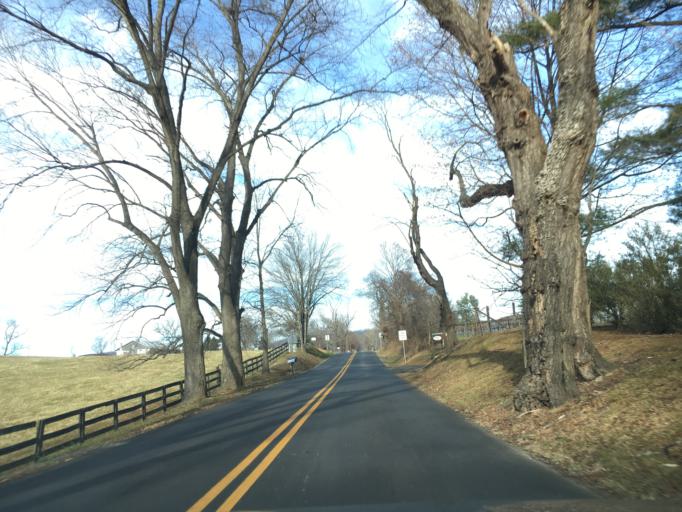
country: US
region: Virginia
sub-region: Warren County
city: Apple Mountain Lake
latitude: 38.8517
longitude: -77.9961
